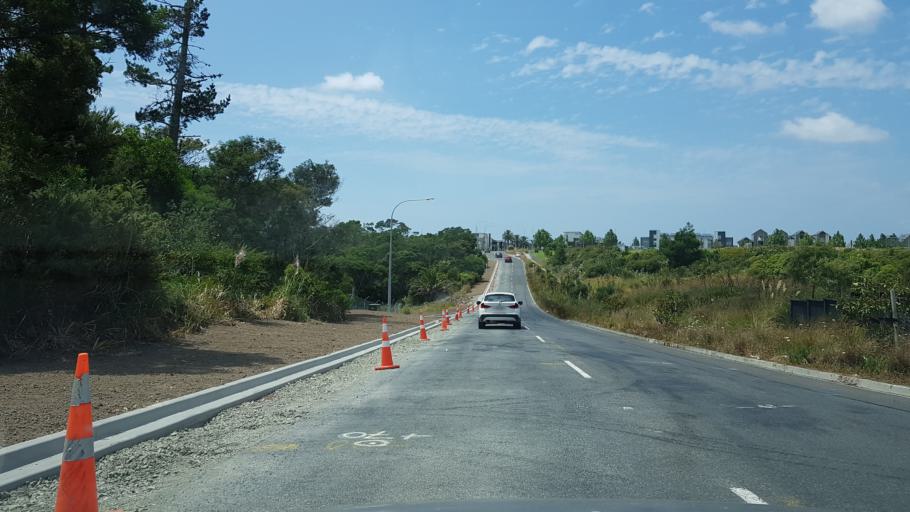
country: NZ
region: Auckland
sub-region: Auckland
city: Rosebank
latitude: -36.7941
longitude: 174.6525
